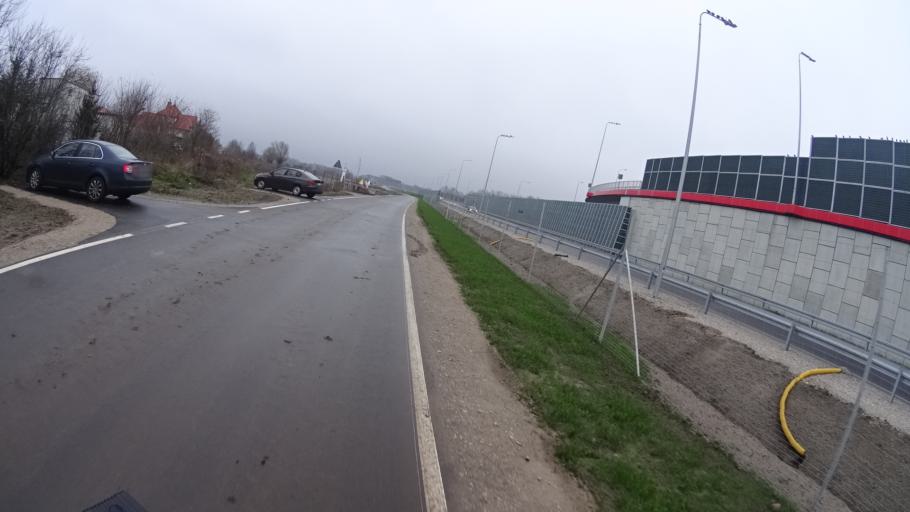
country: PL
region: Masovian Voivodeship
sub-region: Warszawa
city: Wawer
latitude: 52.1642
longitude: 21.1665
